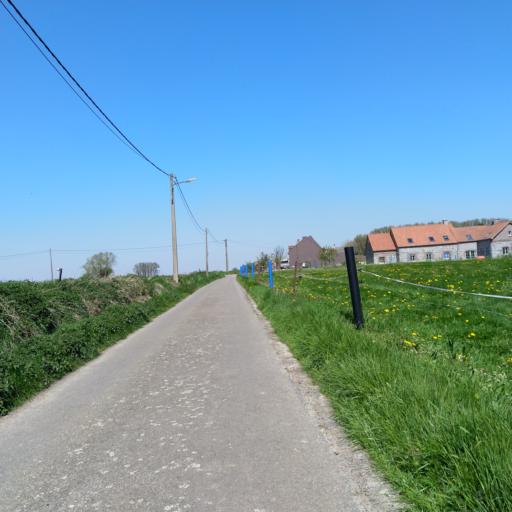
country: BE
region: Wallonia
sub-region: Province du Hainaut
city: Lens
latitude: 50.5480
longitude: 3.8923
